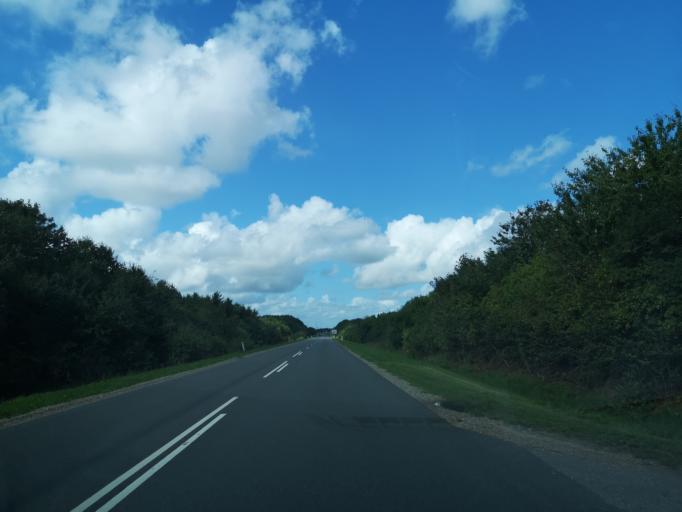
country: DK
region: Central Jutland
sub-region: Holstebro Kommune
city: Holstebro
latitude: 56.3885
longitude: 8.6055
